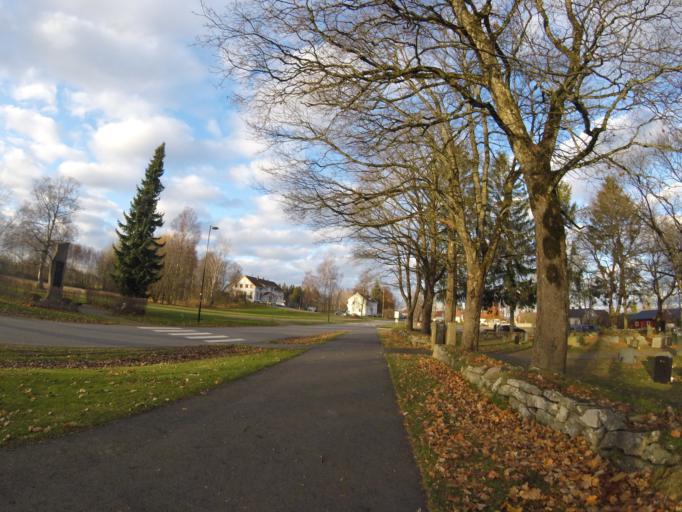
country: NO
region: Akershus
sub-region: Skedsmo
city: Lillestrom
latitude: 59.9940
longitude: 11.0446
